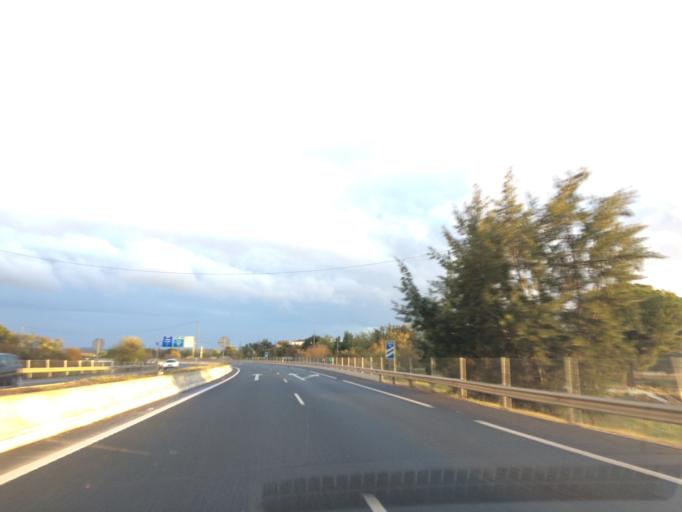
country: ES
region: Andalusia
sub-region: Provincia de Sevilla
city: Alcala de Guadaira
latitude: 37.3328
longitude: -5.8209
